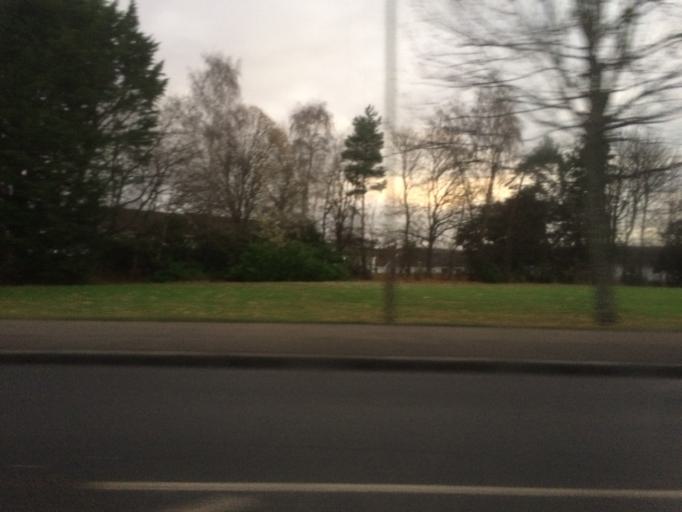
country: GB
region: Scotland
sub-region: Perth and Kinross
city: Perth
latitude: 56.4115
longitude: -3.4542
